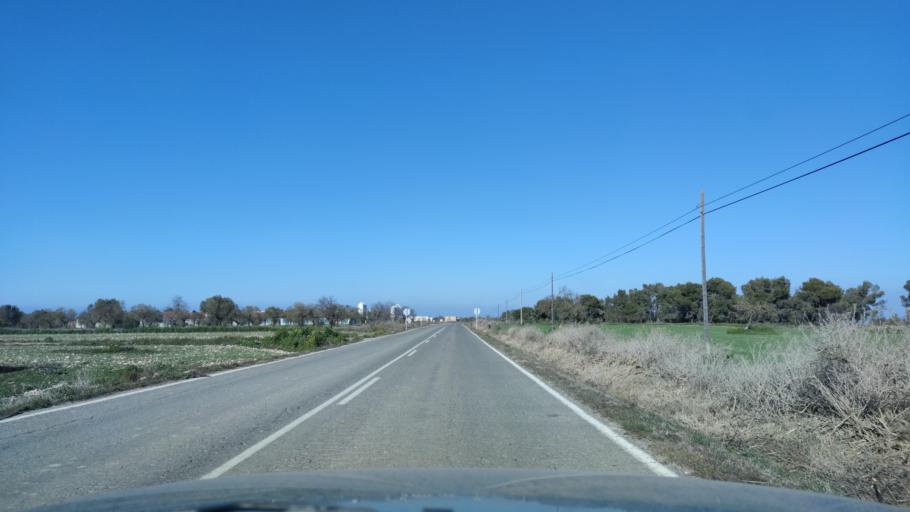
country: ES
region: Catalonia
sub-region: Provincia de Lleida
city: Maials
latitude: 41.3149
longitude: 0.4277
